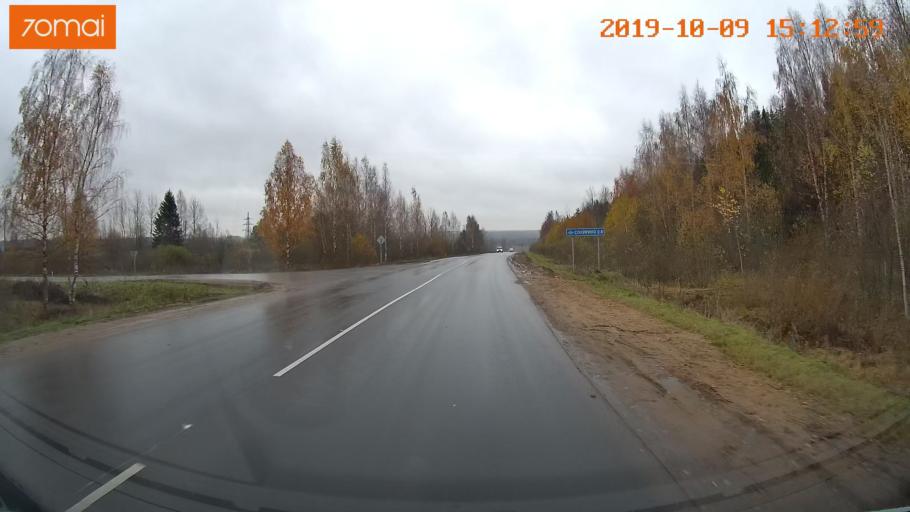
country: RU
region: Kostroma
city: Susanino
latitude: 58.1514
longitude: 41.6148
